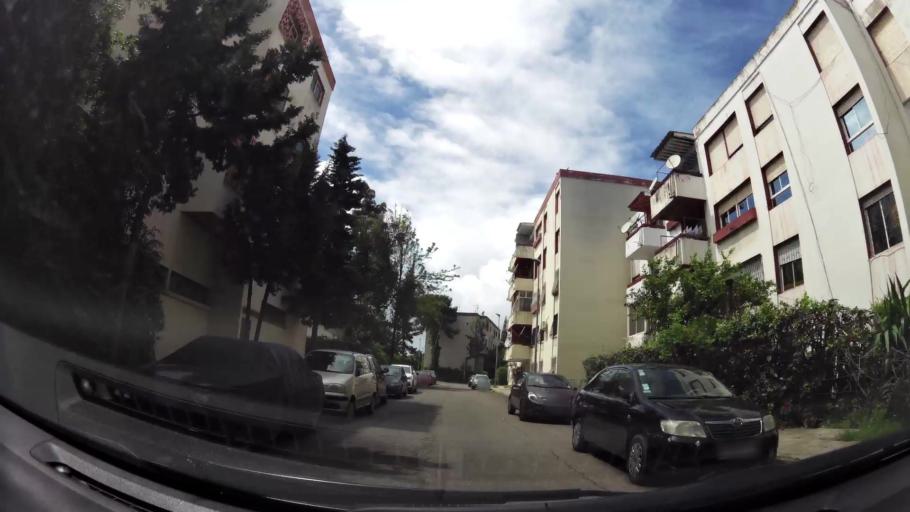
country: MA
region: Grand Casablanca
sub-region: Casablanca
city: Casablanca
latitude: 33.5697
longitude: -7.6326
